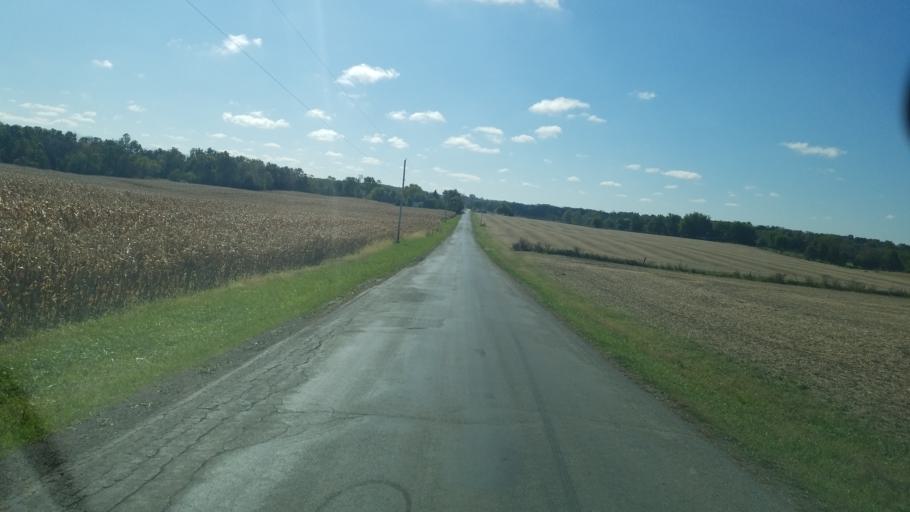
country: US
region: Ohio
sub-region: Highland County
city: Leesburg
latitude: 39.2758
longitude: -83.5542
